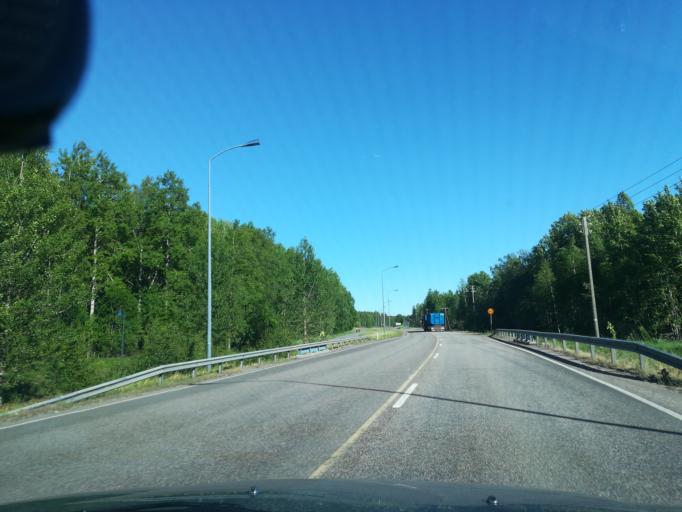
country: FI
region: South Karelia
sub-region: Imatra
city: Imatra
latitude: 61.1578
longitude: 28.7938
